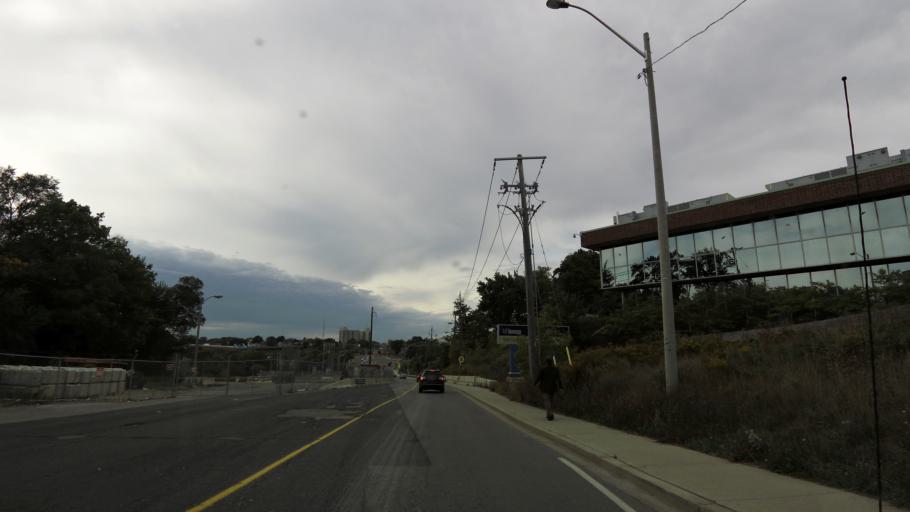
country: CA
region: Ontario
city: Toronto
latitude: 43.6895
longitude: -79.4780
